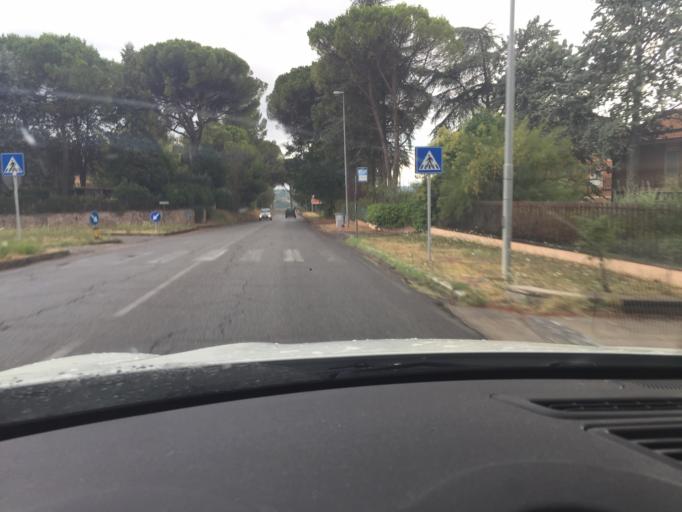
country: IT
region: Umbria
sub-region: Provincia di Perugia
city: Perugia
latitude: 43.0784
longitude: 12.3992
